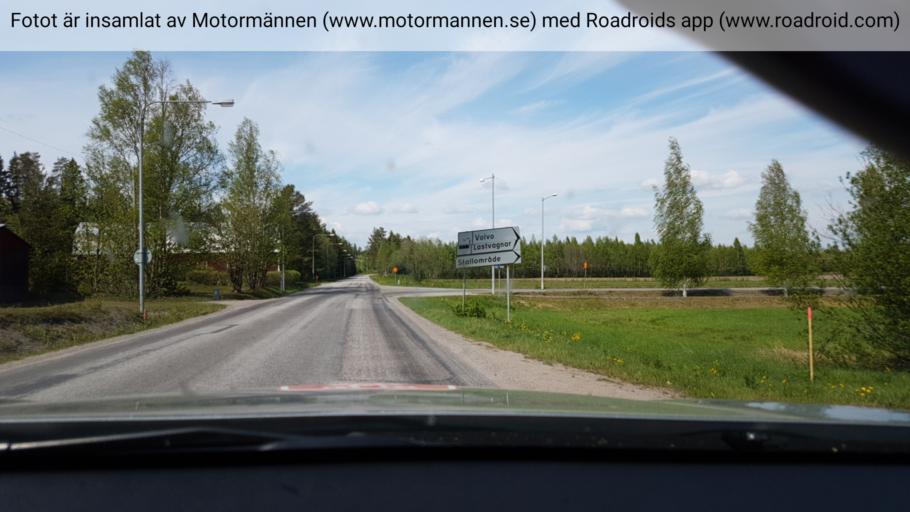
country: SE
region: Vaesterbotten
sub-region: Umea Kommun
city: Roback
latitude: 63.8154
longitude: 20.1828
